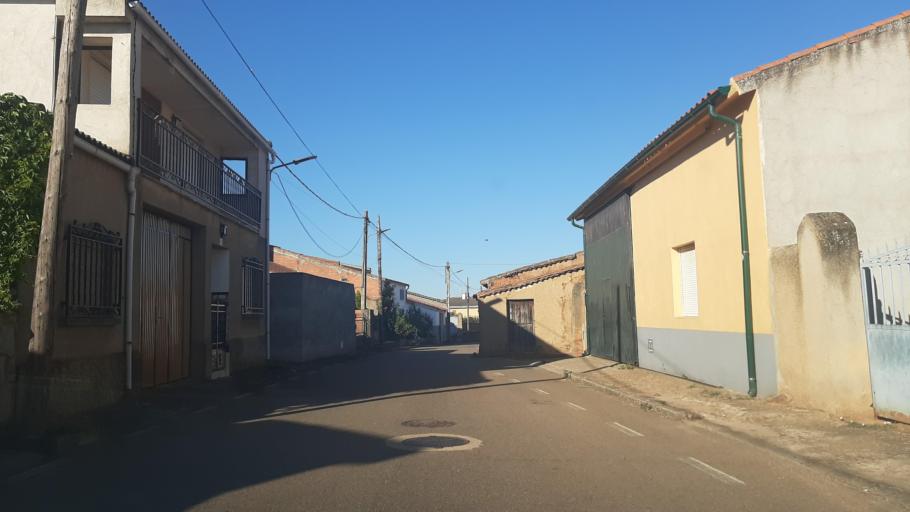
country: ES
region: Castille and Leon
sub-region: Provincia de Salamanca
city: Cabrillas
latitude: 40.6981
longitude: -6.1862
